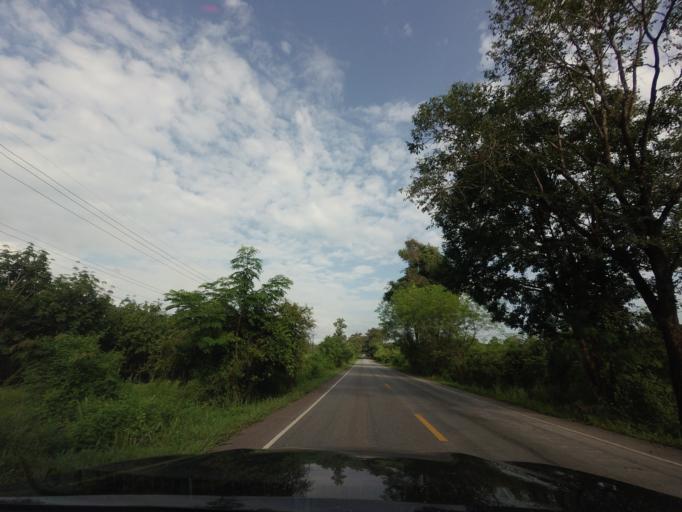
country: TH
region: Nong Khai
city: Pho Tak
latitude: 17.7925
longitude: 102.3575
